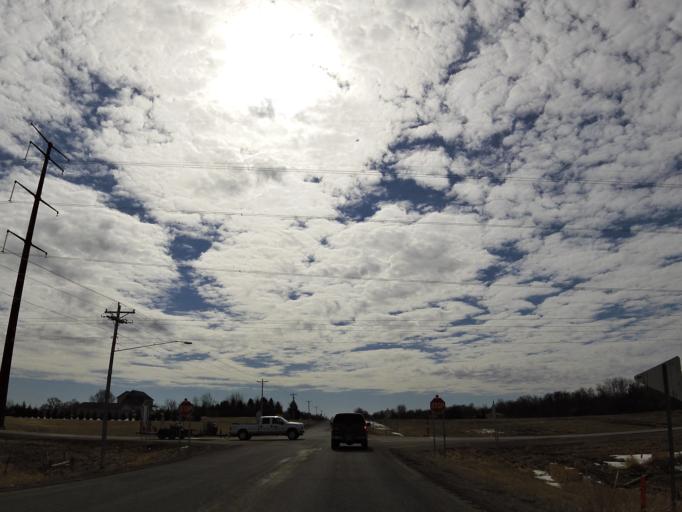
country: US
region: Minnesota
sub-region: Le Sueur County
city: New Prague
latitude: 44.5733
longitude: -93.5570
